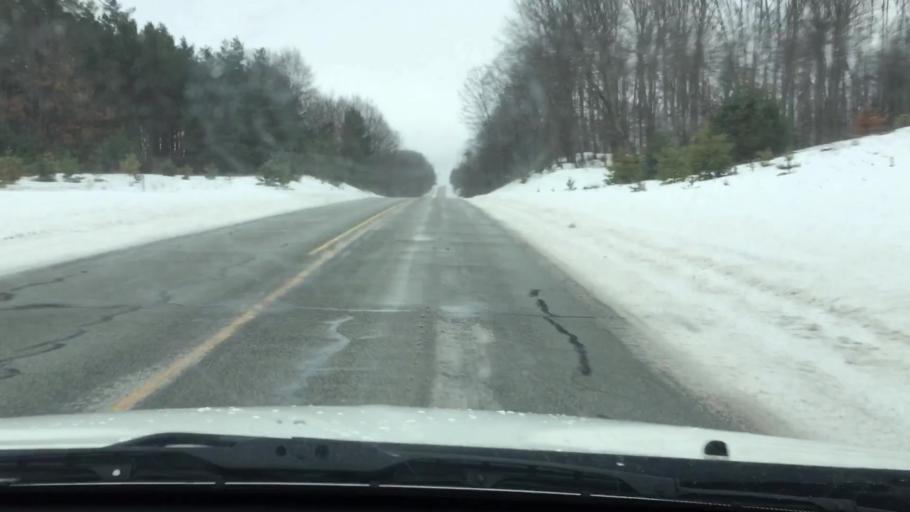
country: US
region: Michigan
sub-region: Wexford County
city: Cadillac
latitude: 44.1748
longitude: -85.4055
